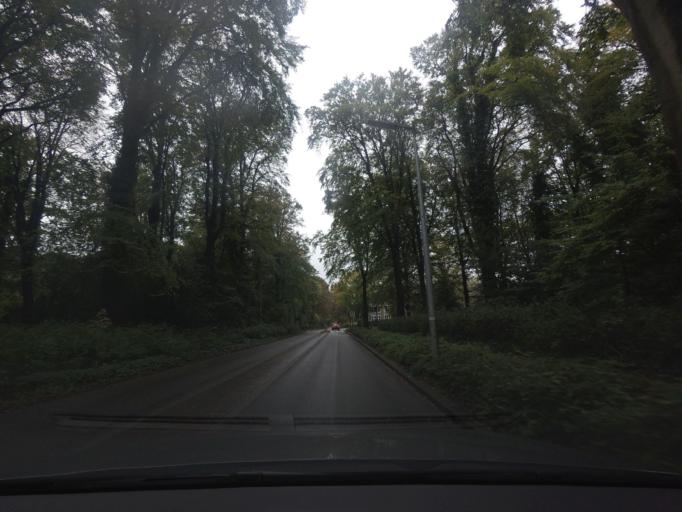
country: NL
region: North Holland
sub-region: Gemeente Alkmaar
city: Alkmaar
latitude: 52.6257
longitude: 4.7359
